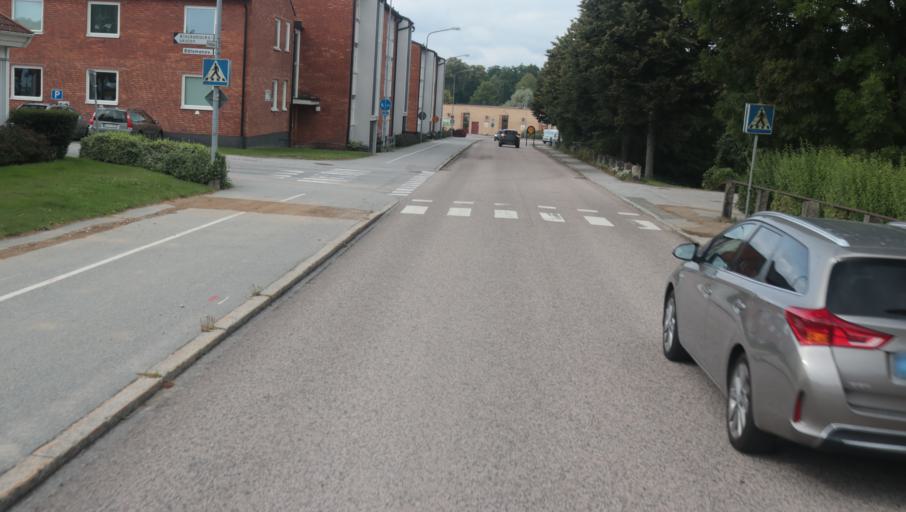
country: SE
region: Blekinge
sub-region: Karlshamns Kommun
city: Karlshamn
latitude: 56.2086
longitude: 14.8363
